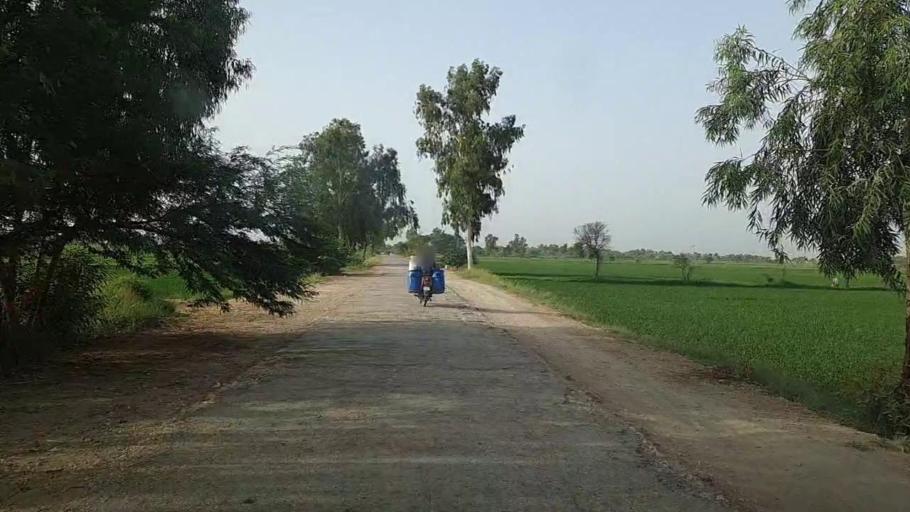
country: PK
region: Sindh
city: Khairpur Nathan Shah
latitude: 27.1256
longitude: 67.7892
